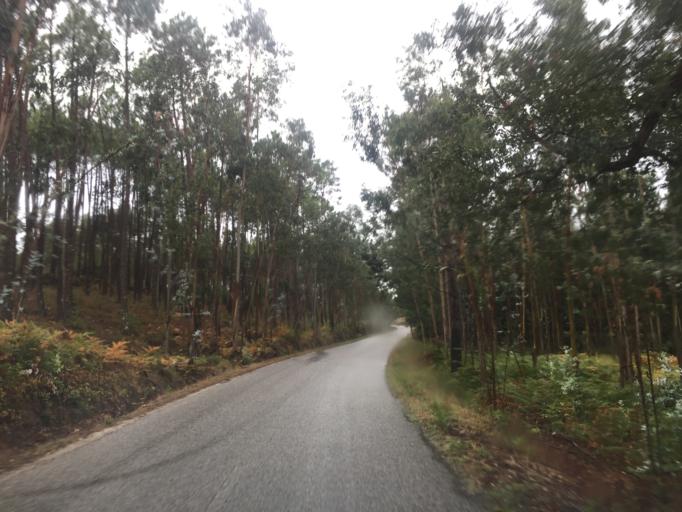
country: PT
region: Leiria
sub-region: Pombal
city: Lourical
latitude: 40.0544
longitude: -8.7737
